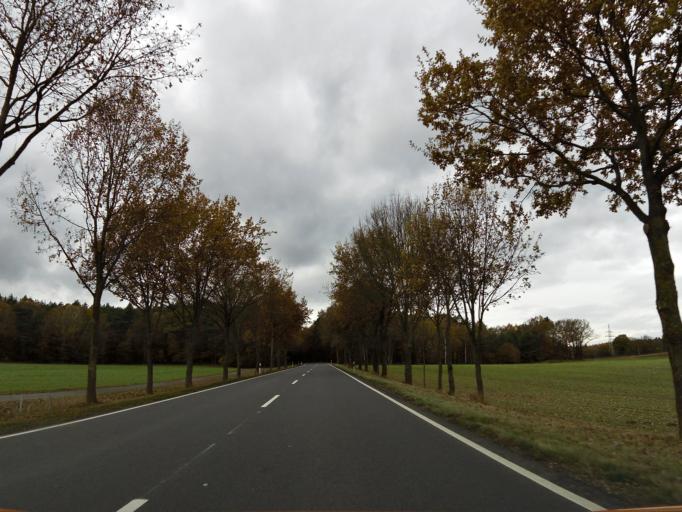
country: DE
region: Lower Saxony
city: Schnega
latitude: 52.9169
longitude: 10.8860
